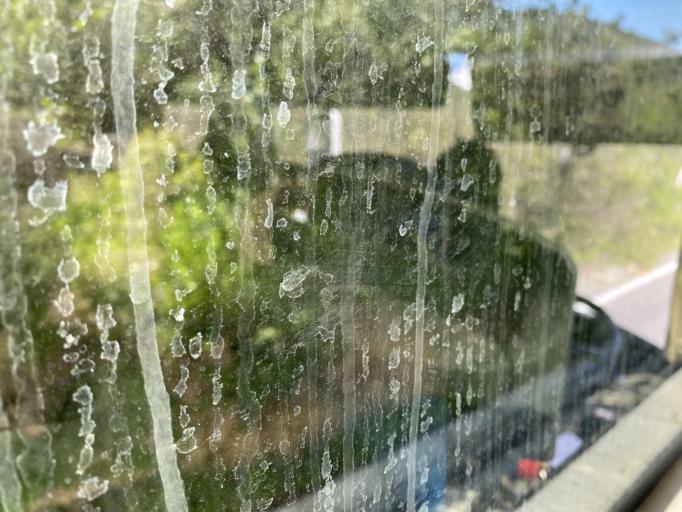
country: CL
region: Valparaiso
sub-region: Provincia de Marga Marga
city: Limache
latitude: -33.1971
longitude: -71.2714
